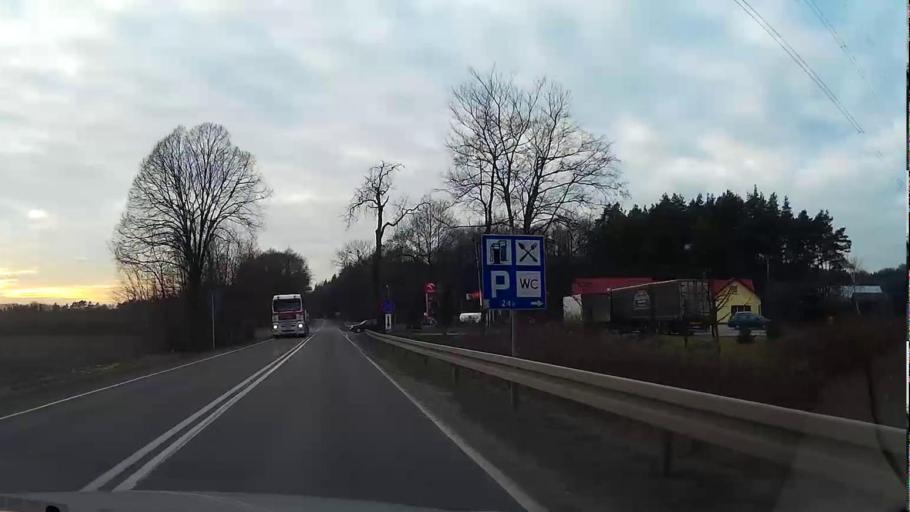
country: PL
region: Lesser Poland Voivodeship
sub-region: Powiat chrzanowski
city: Babice
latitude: 50.0742
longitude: 19.4254
